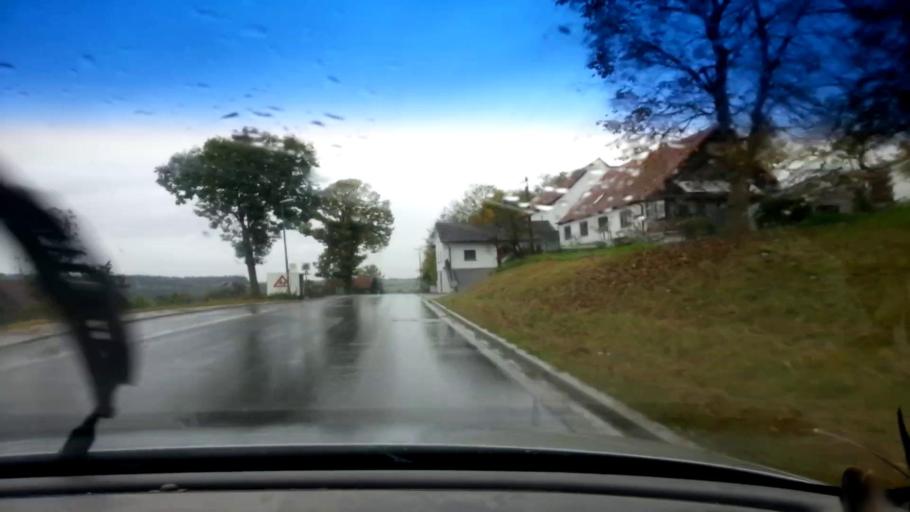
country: DE
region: Bavaria
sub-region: Upper Franconia
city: Konigsfeld
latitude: 49.9331
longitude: 11.1518
